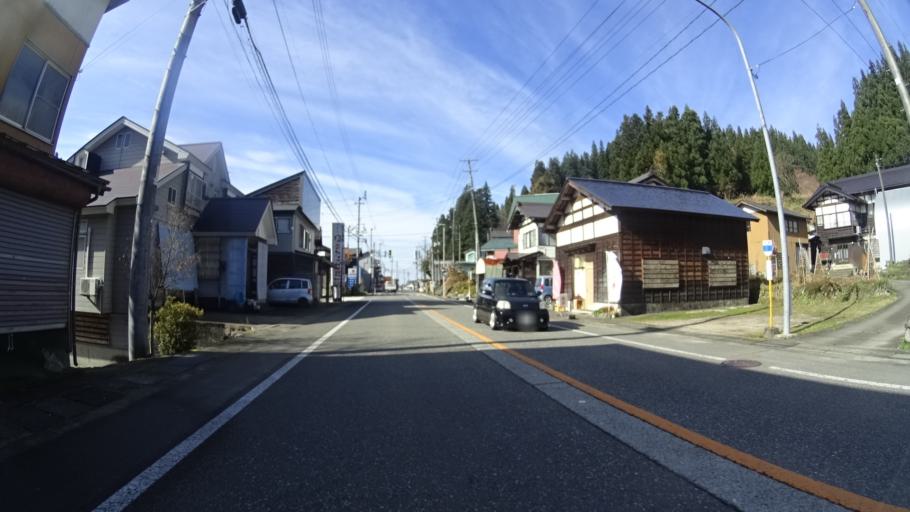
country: JP
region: Niigata
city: Muikamachi
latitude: 37.2078
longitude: 139.0632
